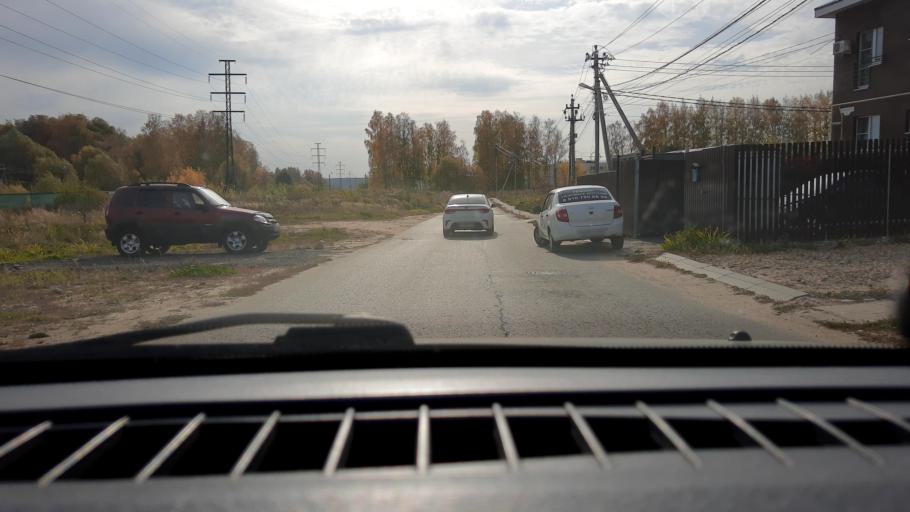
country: RU
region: Nizjnij Novgorod
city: Afonino
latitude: 56.2151
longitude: 44.0913
